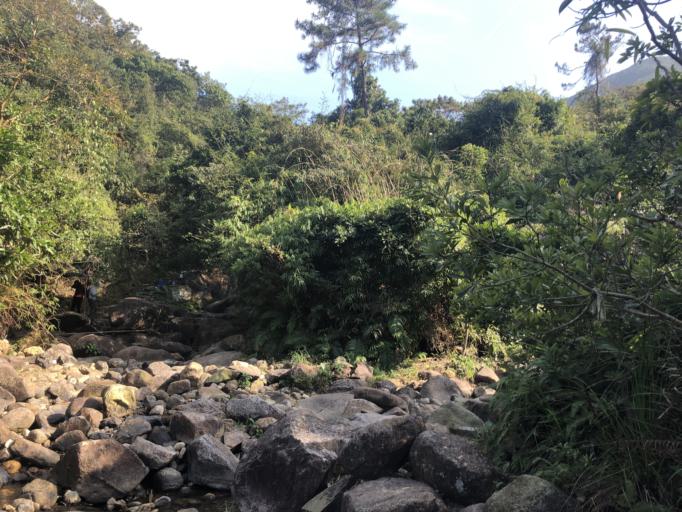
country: HK
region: Wanchai
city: Wan Chai
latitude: 22.2748
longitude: 114.2139
